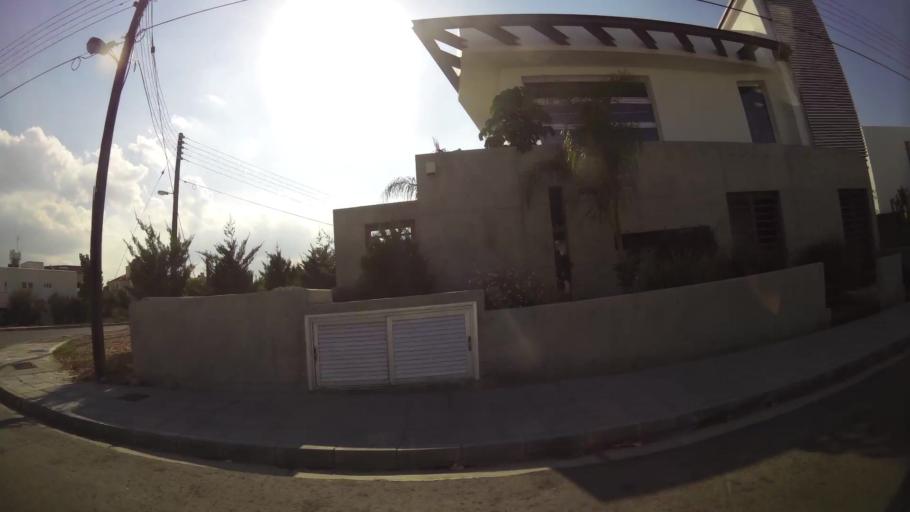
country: CY
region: Lefkosia
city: Nicosia
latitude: 35.1549
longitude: 33.3043
